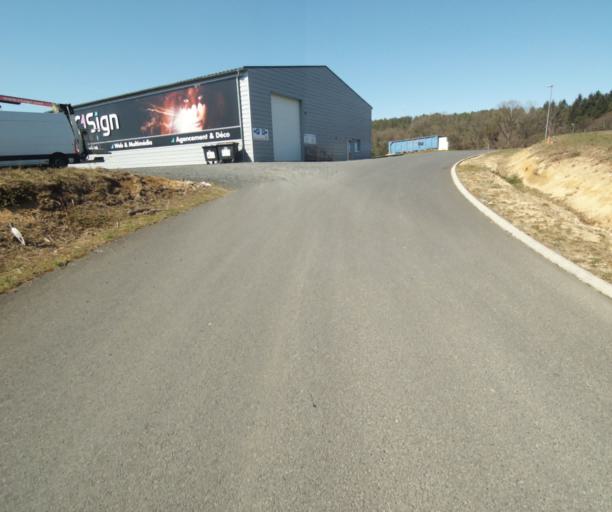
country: FR
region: Limousin
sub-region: Departement de la Correze
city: Saint-Mexant
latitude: 45.2711
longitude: 1.6622
